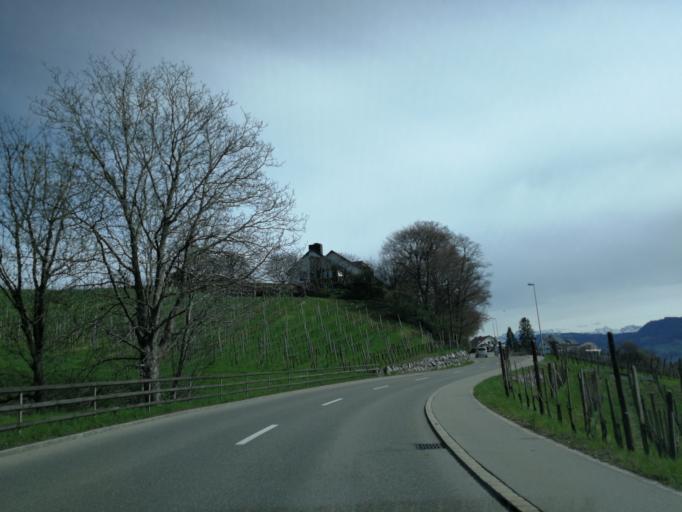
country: CH
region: Zurich
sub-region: Bezirk Meilen
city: Maennedorf / Ausserfeld
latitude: 47.2513
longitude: 8.7128
